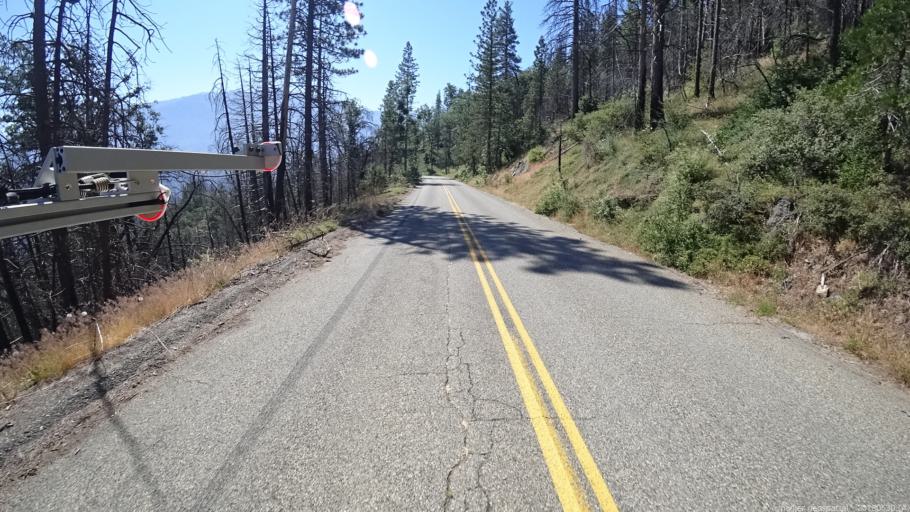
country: US
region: California
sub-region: Fresno County
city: Auberry
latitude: 37.3002
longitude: -119.3501
